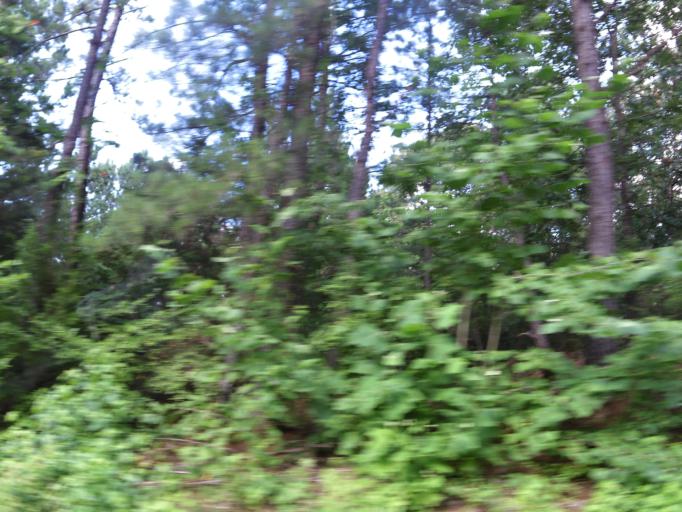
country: US
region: Tennessee
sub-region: Benton County
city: Camden
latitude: 36.0564
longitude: -88.1661
